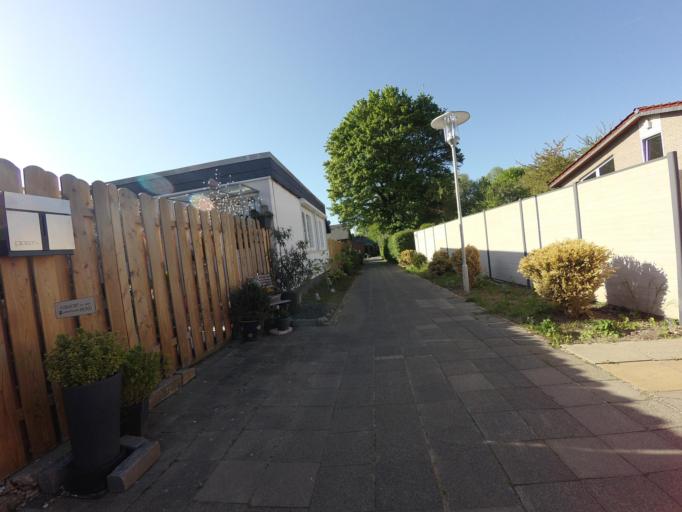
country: DE
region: Lower Saxony
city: Hildesheim
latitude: 52.1411
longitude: 9.9222
